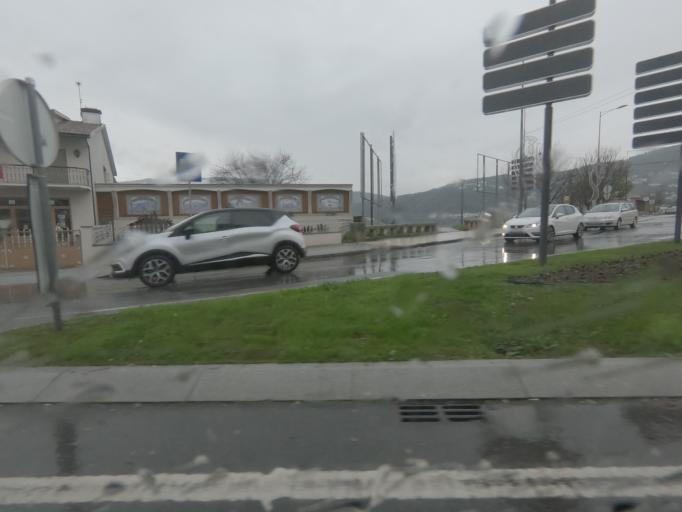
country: PT
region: Vila Real
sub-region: Peso da Regua
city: Peso da Regua
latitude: 41.1620
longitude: -7.7917
